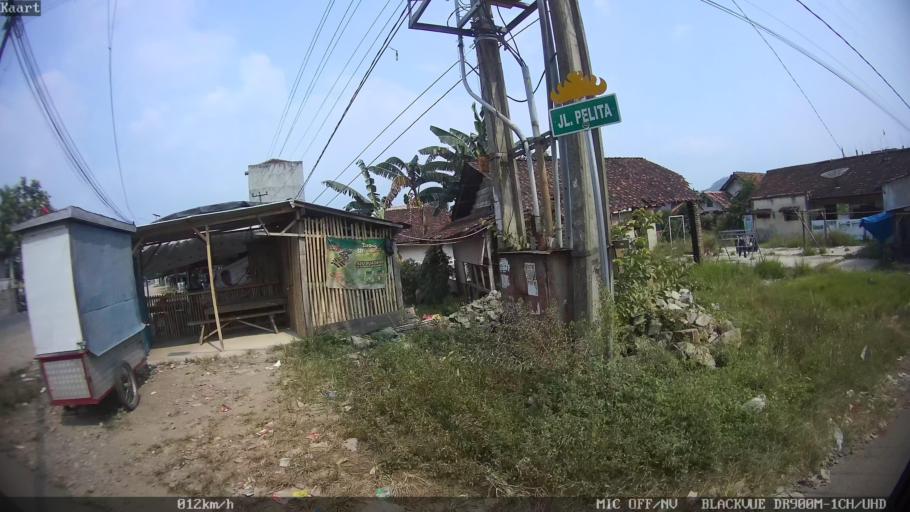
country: ID
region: Lampung
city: Pringsewu
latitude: -5.3635
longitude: 105.0032
